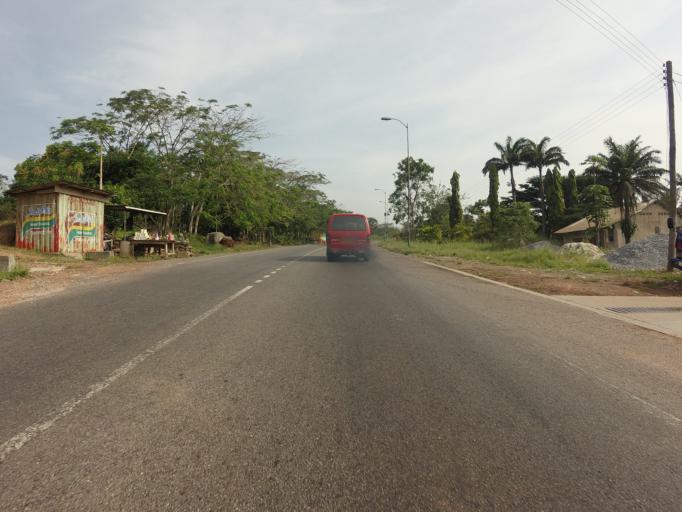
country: GH
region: Eastern
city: Aburi
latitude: 5.8308
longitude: -0.1842
